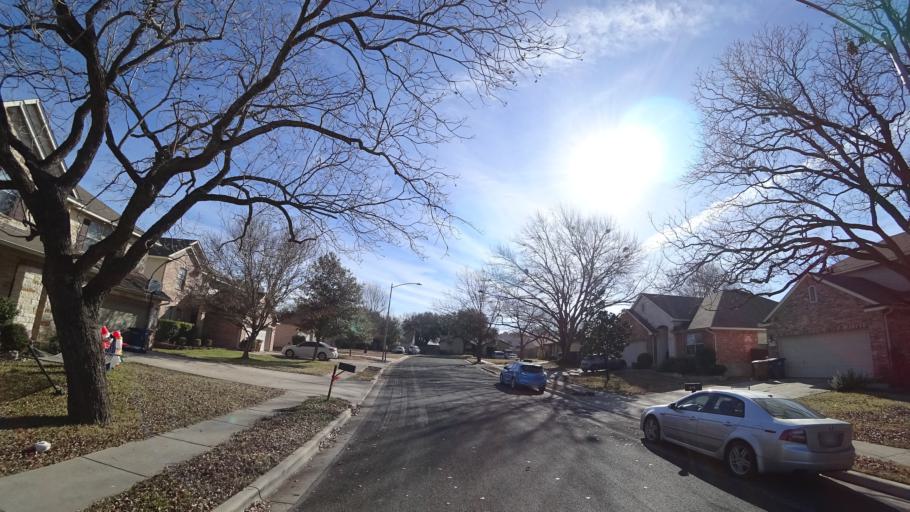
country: US
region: Texas
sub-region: Travis County
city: Wells Branch
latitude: 30.3907
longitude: -97.6938
